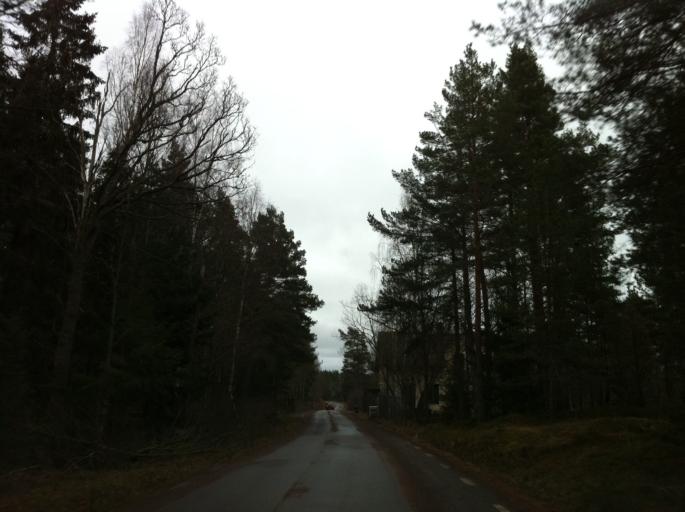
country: SE
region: Kalmar
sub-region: Vasterviks Kommun
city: Forserum
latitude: 57.9258
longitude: 16.5477
